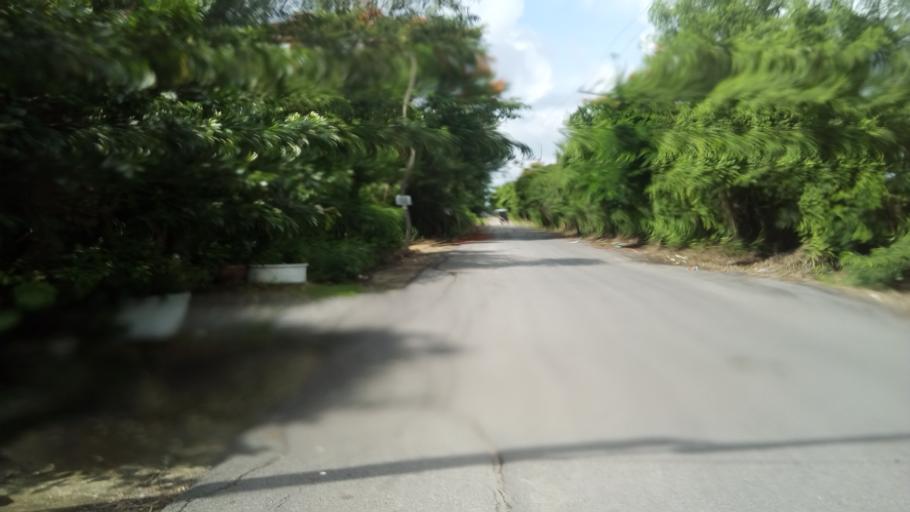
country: TH
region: Pathum Thani
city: Nong Suea
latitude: 14.0645
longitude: 100.8631
